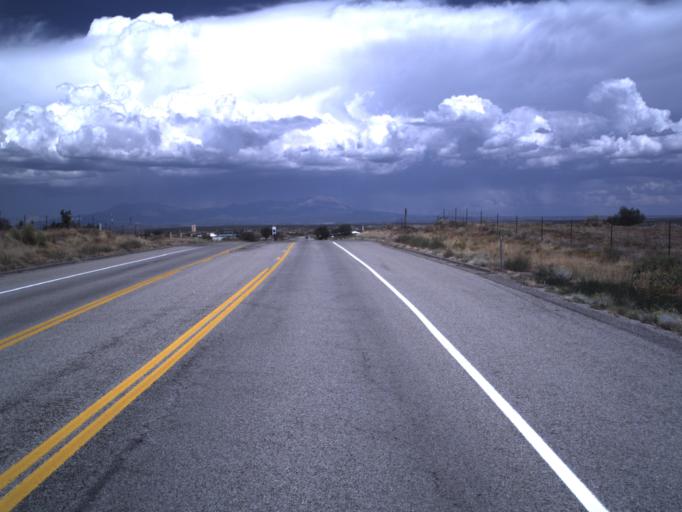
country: US
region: Utah
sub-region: San Juan County
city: Blanding
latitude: 37.4594
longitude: -109.4670
